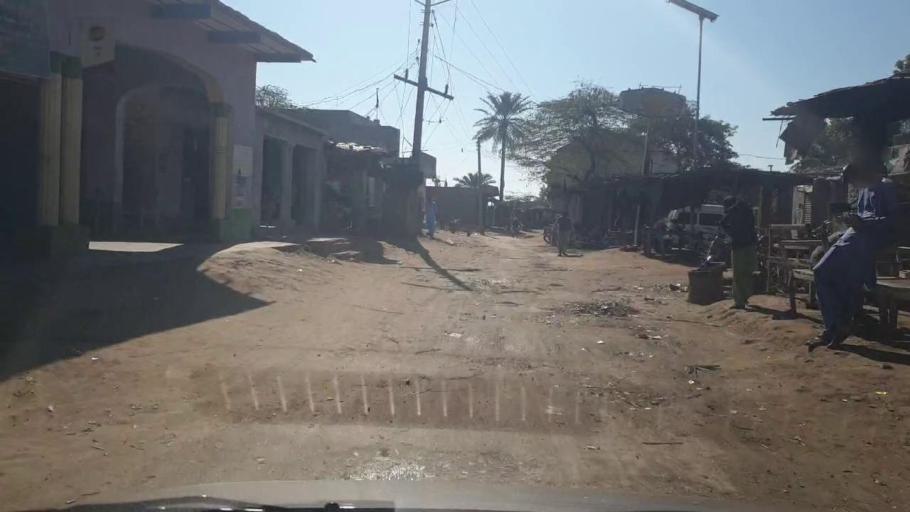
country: PK
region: Sindh
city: Bozdar
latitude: 27.2458
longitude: 68.6521
